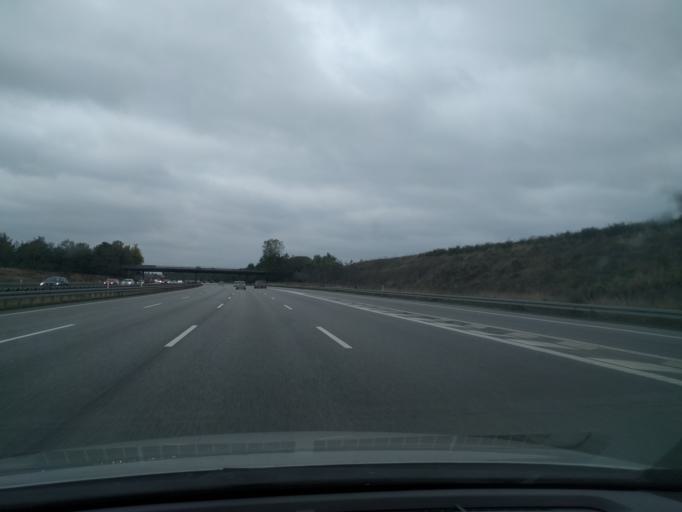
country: DK
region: Zealand
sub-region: Koge Kommune
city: Ejby
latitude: 55.4960
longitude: 12.1290
